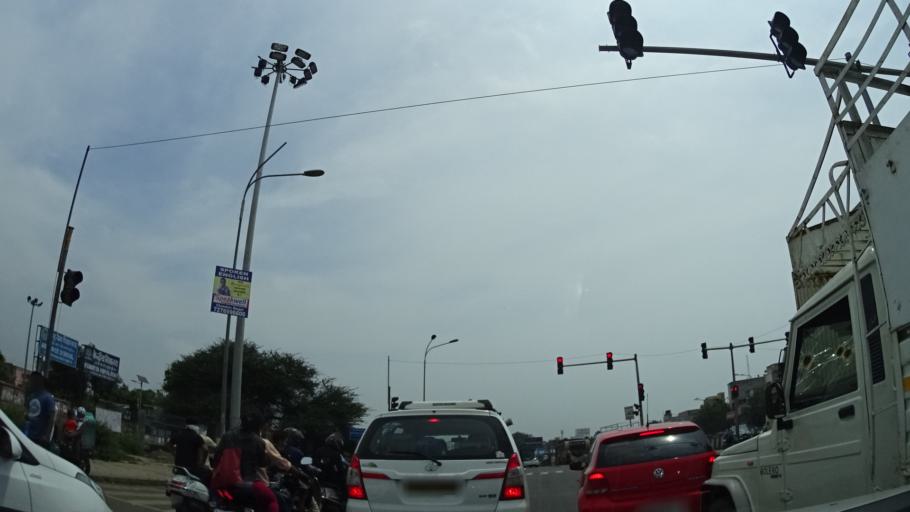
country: IN
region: Maharashtra
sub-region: Pune Division
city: Lohogaon
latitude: 18.5633
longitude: 73.9320
